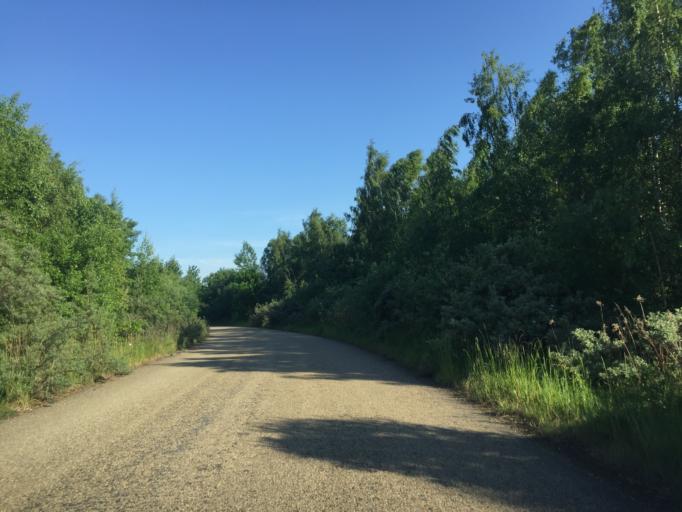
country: DK
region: Capital Region
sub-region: Kobenhavn
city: Copenhagen
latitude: 55.6310
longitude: 12.5486
